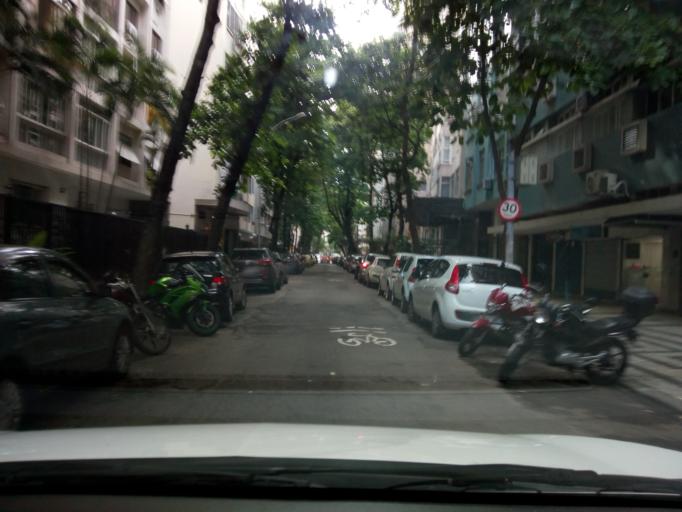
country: BR
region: Rio de Janeiro
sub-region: Rio De Janeiro
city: Rio de Janeiro
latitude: -22.9701
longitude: -43.1842
